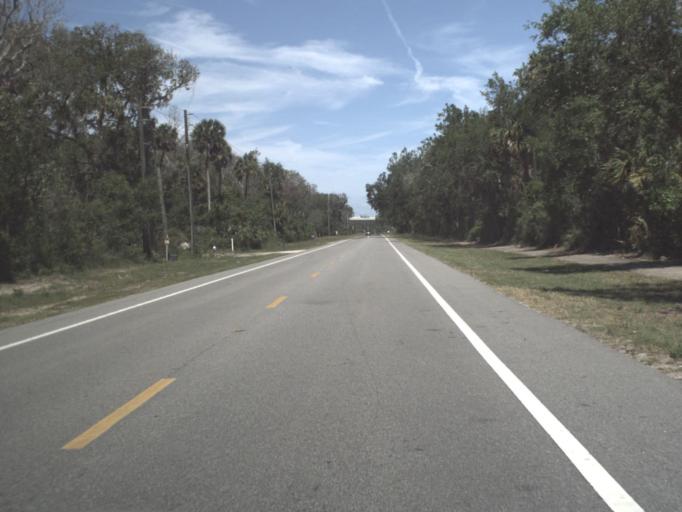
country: US
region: Florida
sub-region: Flagler County
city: Palm Coast
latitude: 29.5708
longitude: -81.1840
